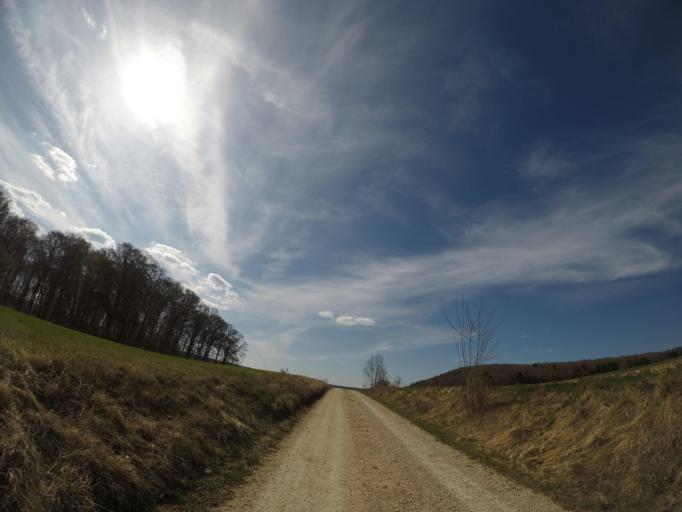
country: DE
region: Baden-Wuerttemberg
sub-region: Tuebingen Region
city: Mehrstetten
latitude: 48.3212
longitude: 9.5762
